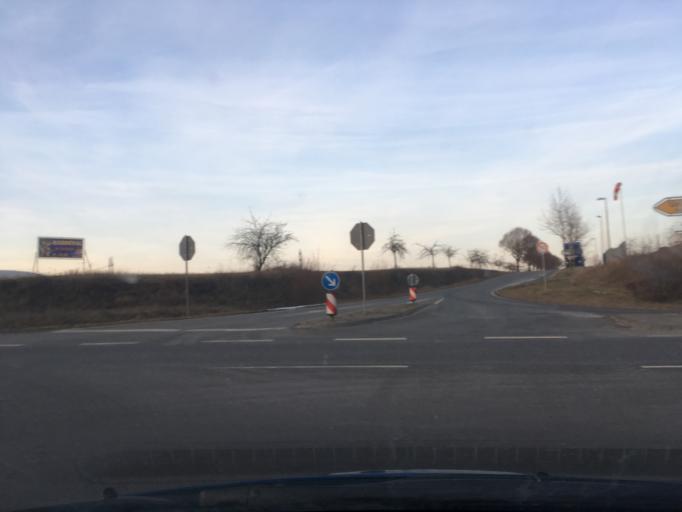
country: DE
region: Lower Saxony
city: Hardegsen
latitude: 51.6447
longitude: 9.8597
